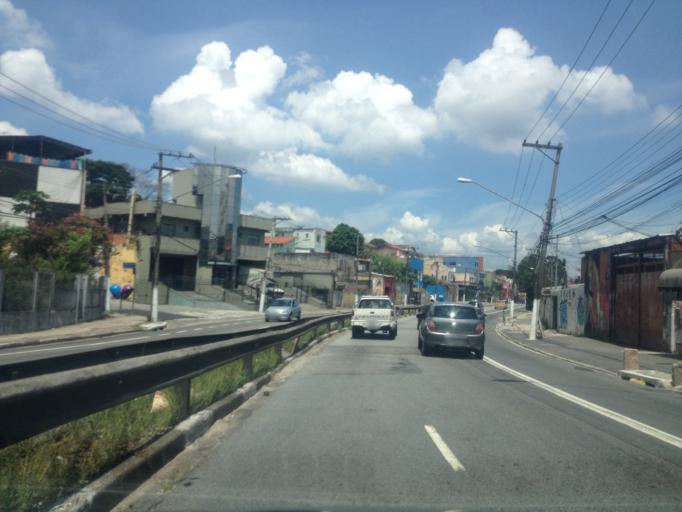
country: BR
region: Sao Paulo
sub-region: Diadema
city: Diadema
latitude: -23.6763
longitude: -46.6797
